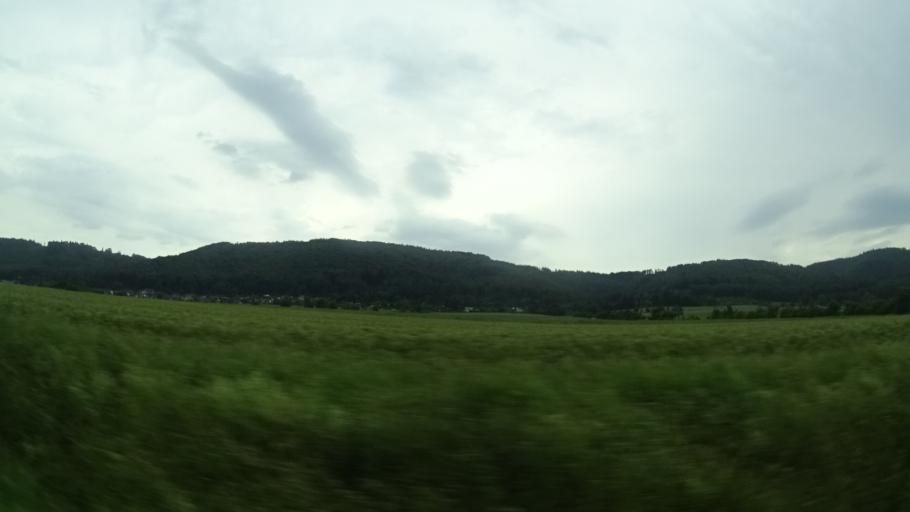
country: DE
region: Lower Saxony
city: Bodenwerder
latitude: 51.9601
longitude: 9.5113
